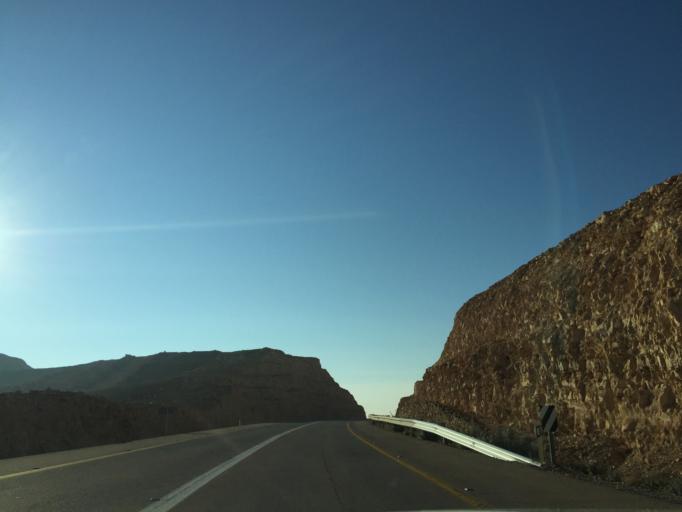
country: IL
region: Southern District
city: Mitzpe Ramon
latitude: 30.3823
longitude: 34.9504
